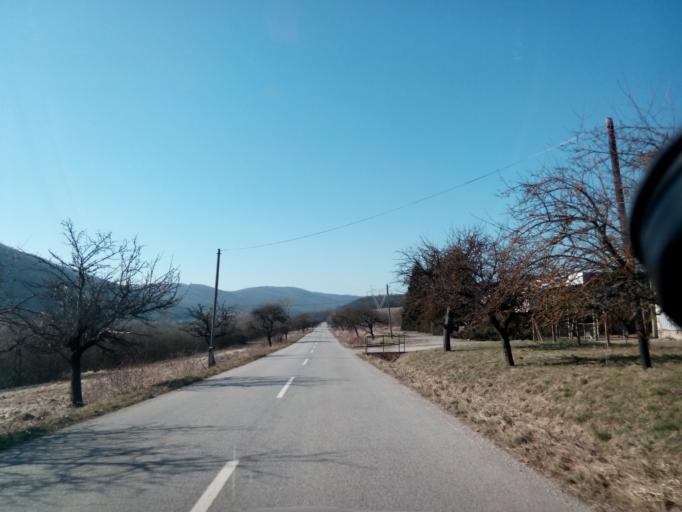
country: SK
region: Kosicky
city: Roznava
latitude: 48.5835
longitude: 20.6610
